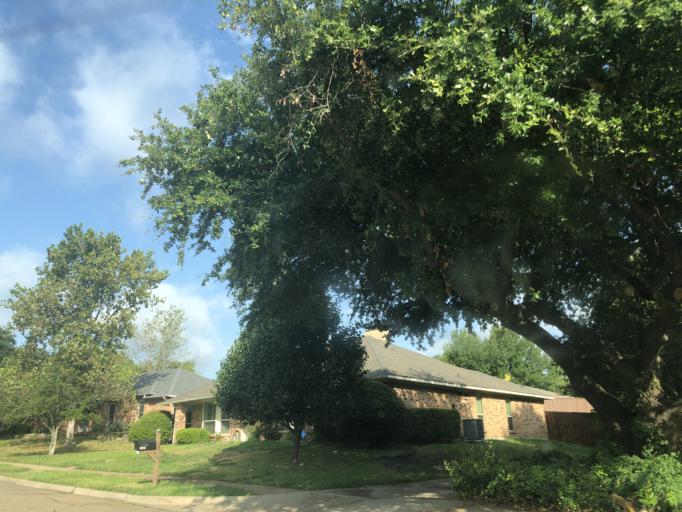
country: US
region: Texas
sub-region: Dallas County
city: Garland
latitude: 32.8600
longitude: -96.6243
